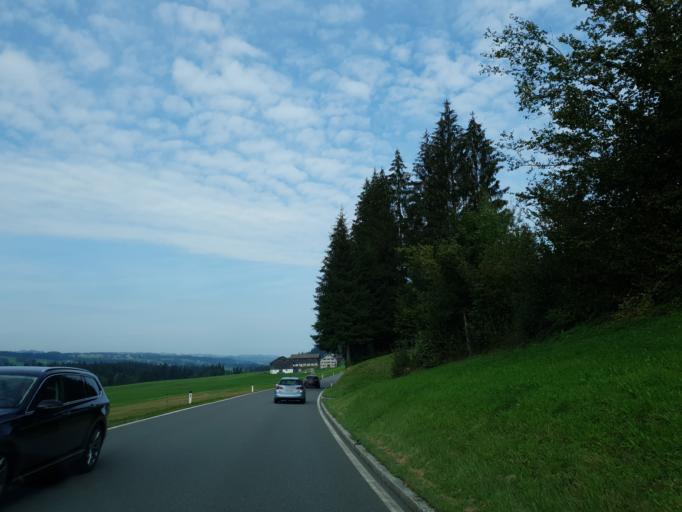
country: AT
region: Vorarlberg
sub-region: Politischer Bezirk Bregenz
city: Doren
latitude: 47.5000
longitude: 9.8603
